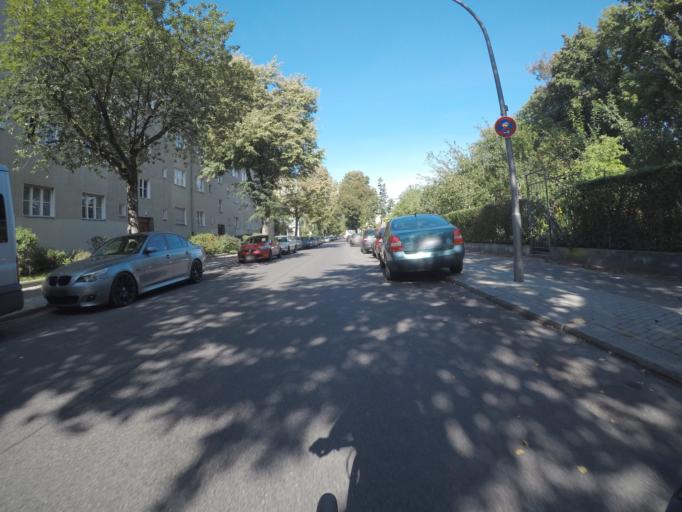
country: DE
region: Berlin
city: Pankow
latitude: 52.5603
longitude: 13.3963
